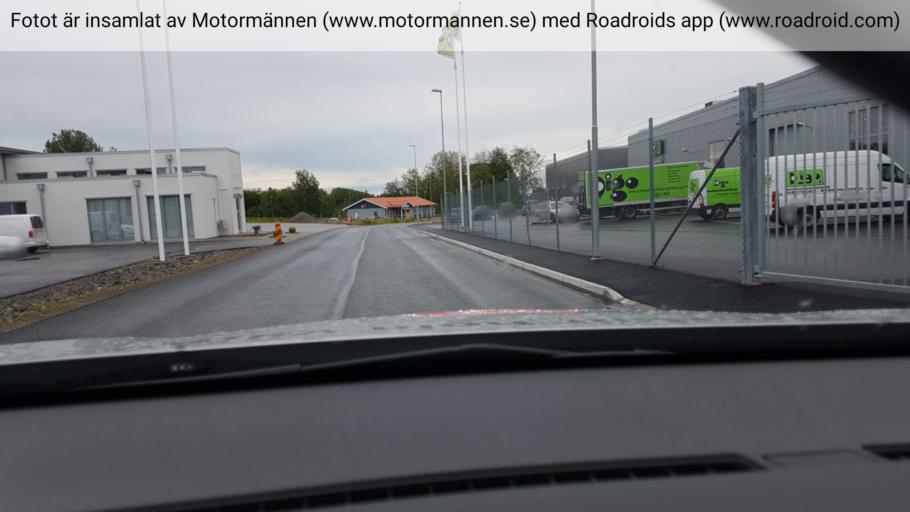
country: SE
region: Vaestra Goetaland
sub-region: Skovde Kommun
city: Skoevde
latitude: 58.3996
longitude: 13.8780
